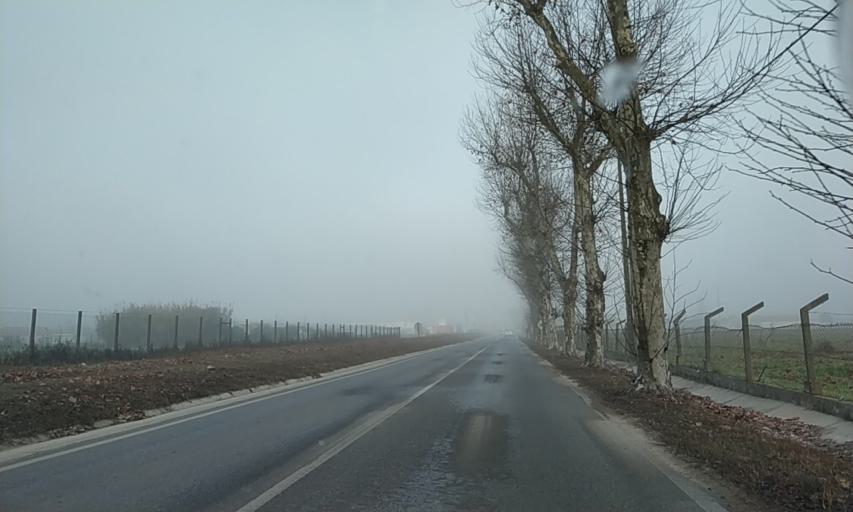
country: PT
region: Setubal
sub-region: Palmela
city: Pinhal Novo
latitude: 38.6578
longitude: -8.9206
